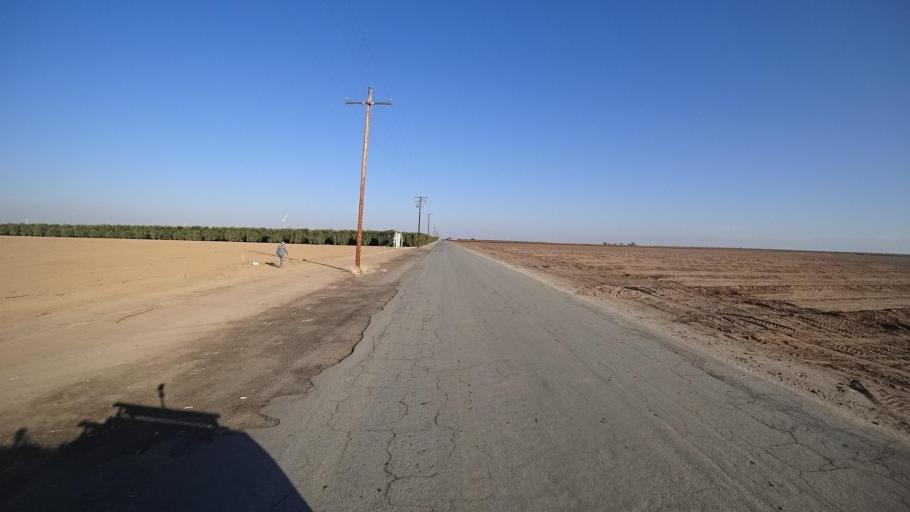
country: US
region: California
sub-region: Tulare County
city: Richgrove
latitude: 35.7643
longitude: -119.1519
